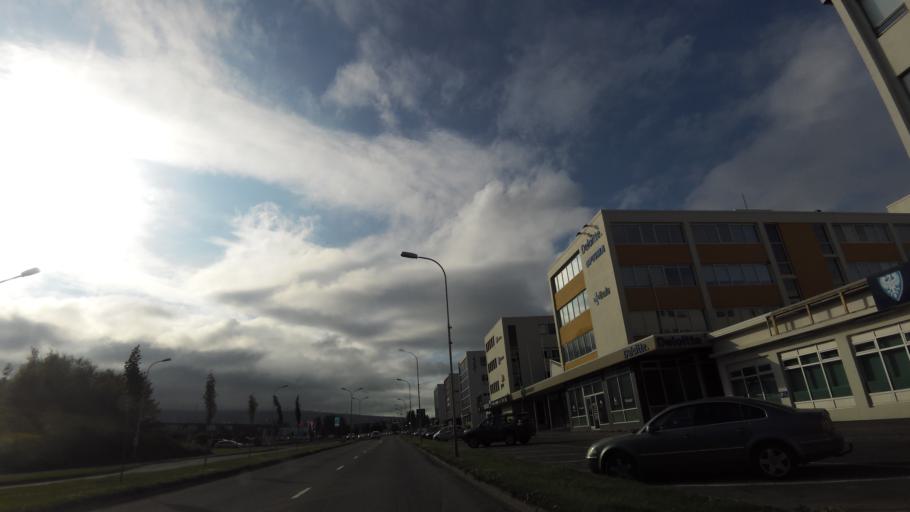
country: IS
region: Northeast
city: Akureyri
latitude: 65.6874
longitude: -18.0968
